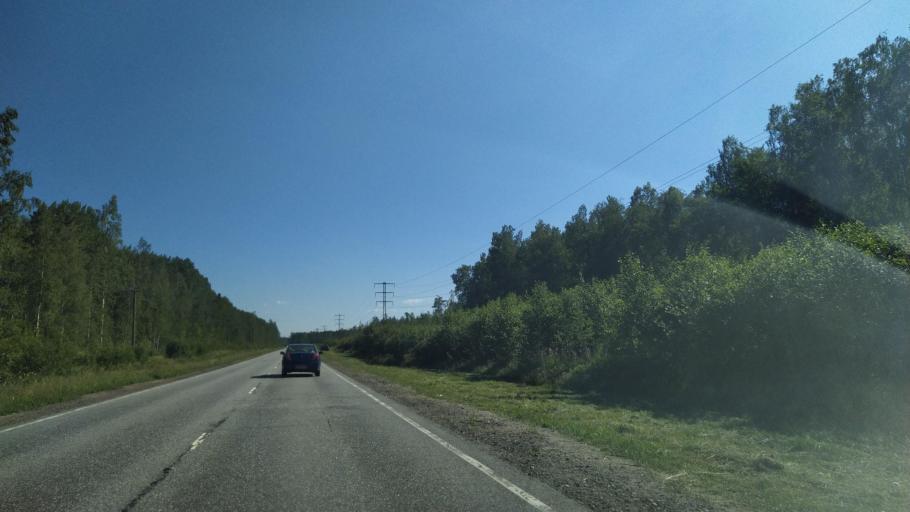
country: RU
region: Leningrad
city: Imeni Morozova
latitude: 60.0387
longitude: 31.0361
